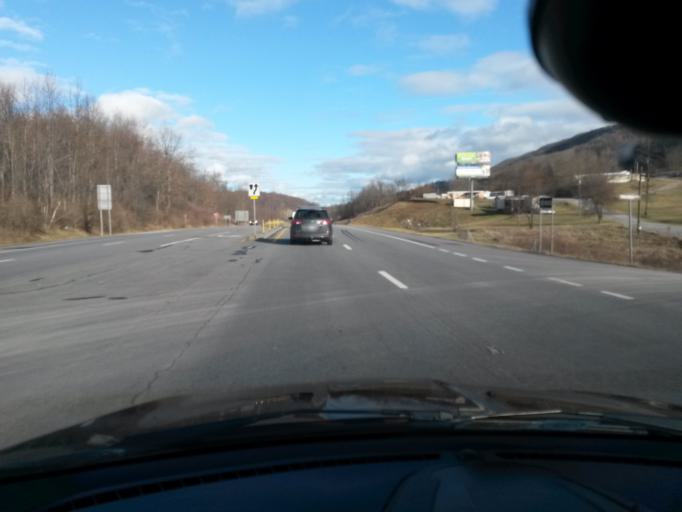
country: US
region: West Virginia
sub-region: Mercer County
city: Princeton
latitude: 37.2821
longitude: -81.1330
